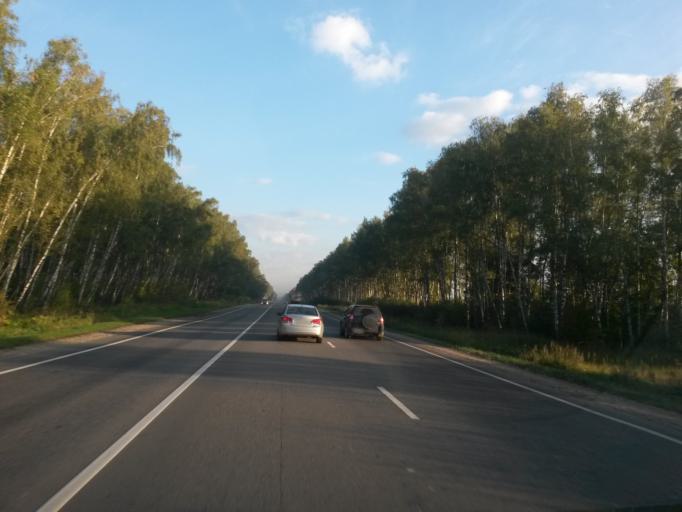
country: RU
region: Moskovskaya
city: Belyye Stolby
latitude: 55.2841
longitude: 37.8225
